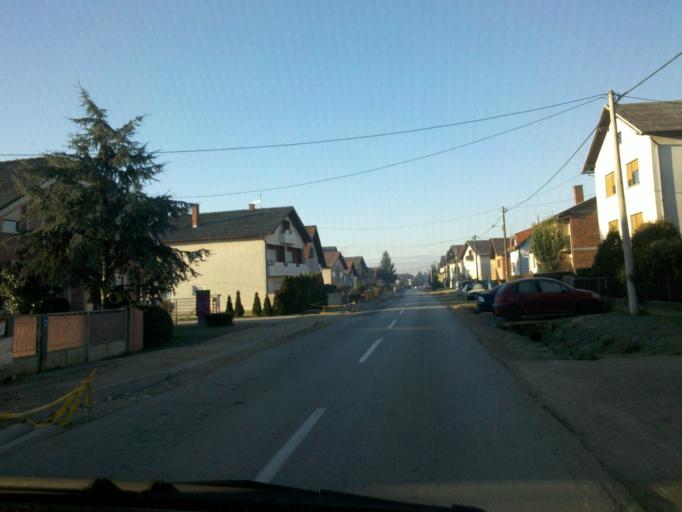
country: HR
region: Medimurska
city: Belica
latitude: 46.4056
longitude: 16.5115
